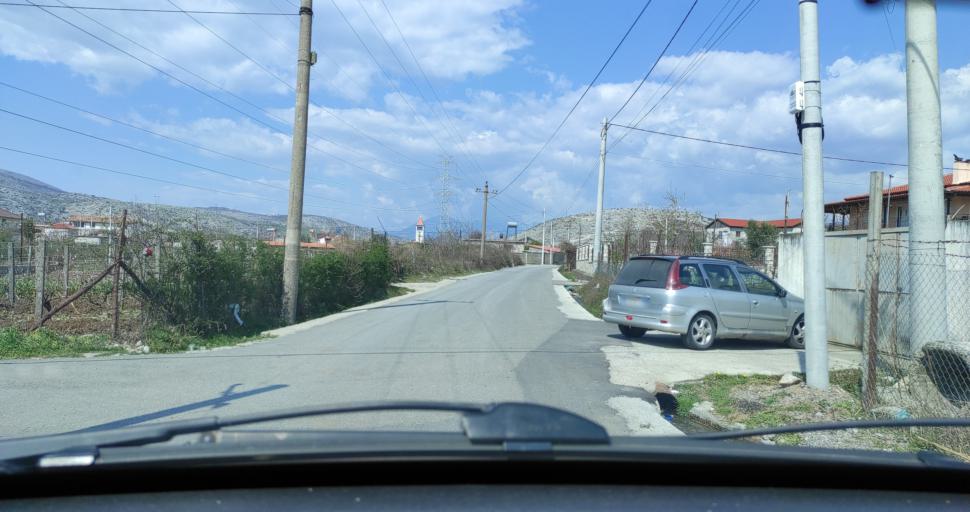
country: AL
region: Shkoder
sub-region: Rrethi i Shkodres
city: Vau i Dejes
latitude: 42.0029
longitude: 19.6420
